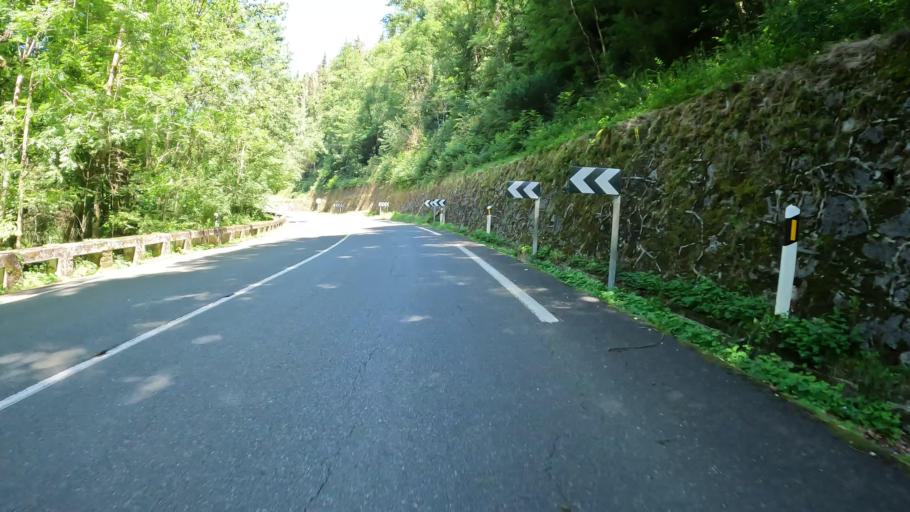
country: ES
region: Basque Country
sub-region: Provincia de Guipuzcoa
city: Oreja
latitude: 43.0739
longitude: -2.0118
